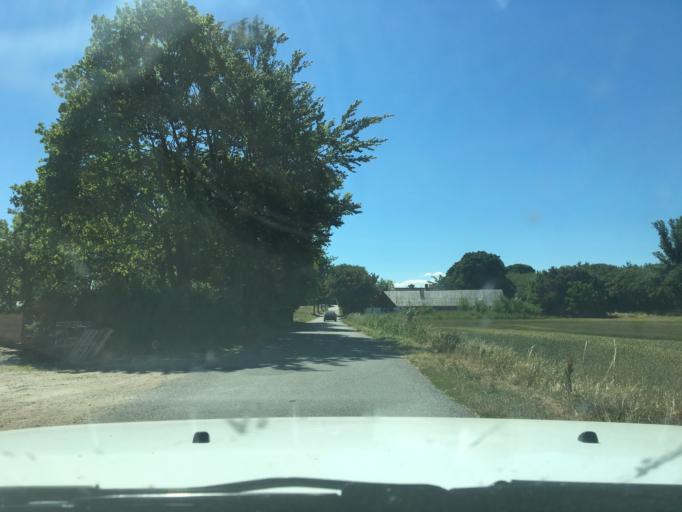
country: DK
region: Central Jutland
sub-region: Syddjurs Kommune
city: Hornslet
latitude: 56.3449
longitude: 10.3864
